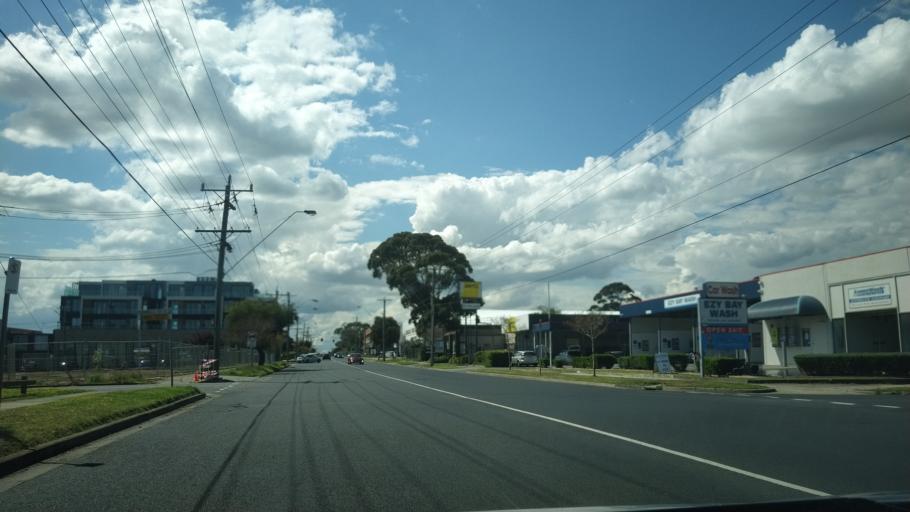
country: AU
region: Victoria
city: Highett
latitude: -37.9441
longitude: 145.0597
